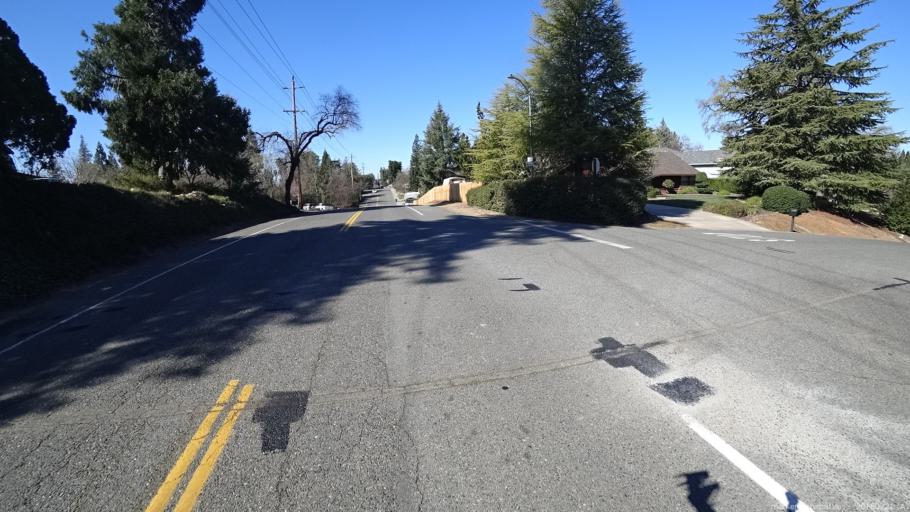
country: US
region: California
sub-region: Sacramento County
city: Orangevale
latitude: 38.6932
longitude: -121.2410
